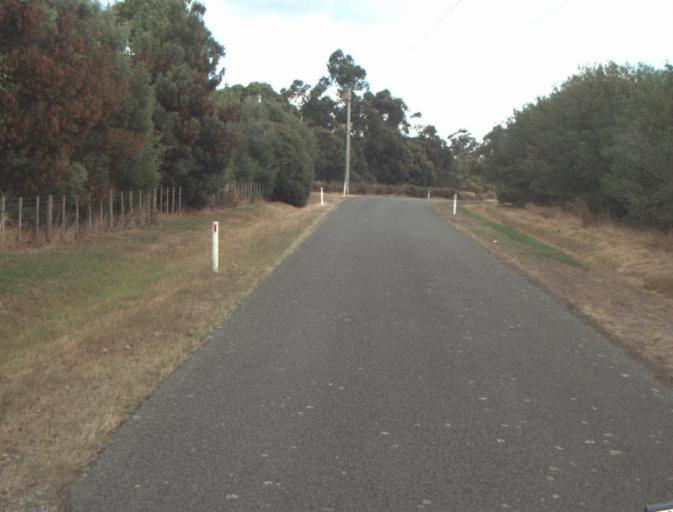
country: AU
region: Tasmania
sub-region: Launceston
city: Mayfield
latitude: -41.2937
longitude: 146.9905
